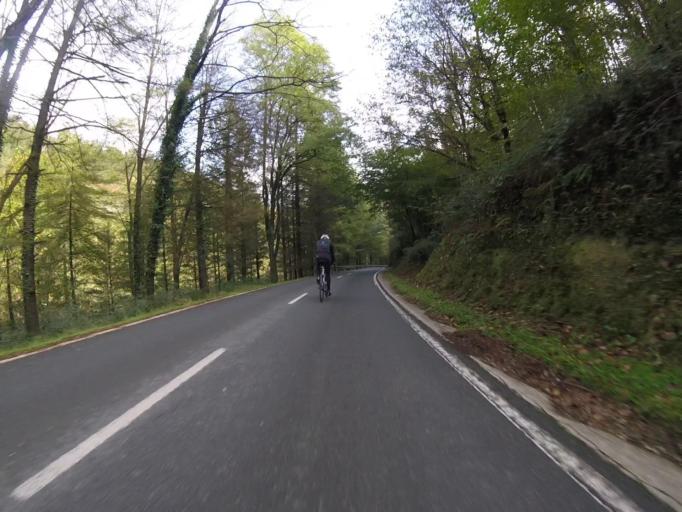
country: ES
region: Navarre
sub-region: Provincia de Navarra
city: Goizueta
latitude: 43.1943
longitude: -1.8588
